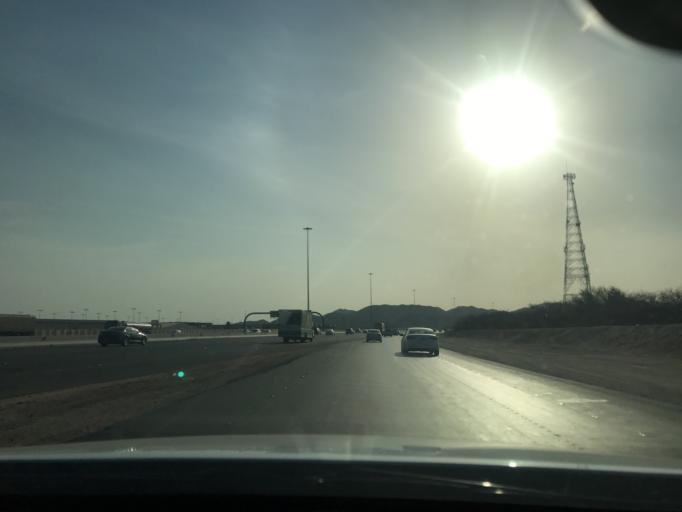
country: SA
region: Makkah
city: Jeddah
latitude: 21.3895
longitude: 39.4239
